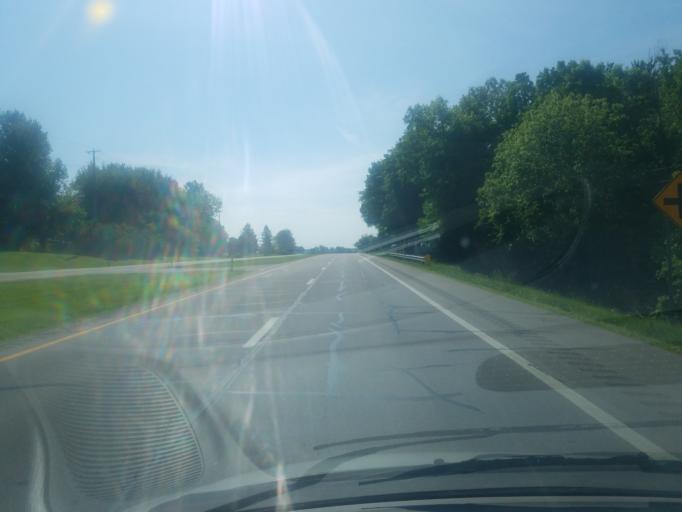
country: US
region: Ohio
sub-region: Huron County
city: Monroeville
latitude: 41.2611
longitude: -82.7680
